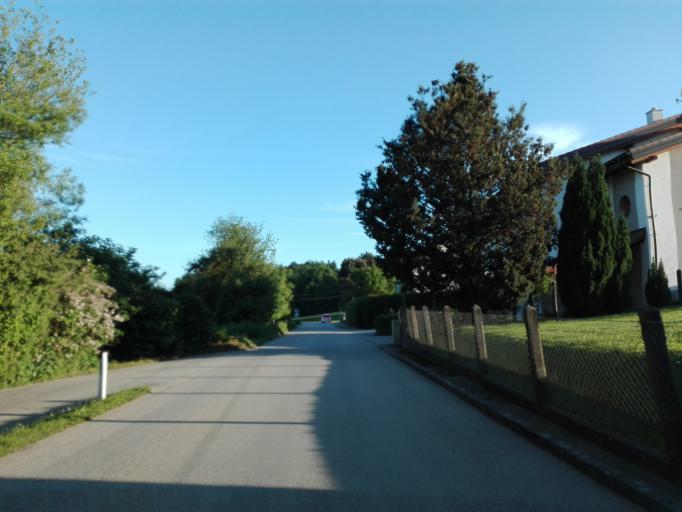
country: AT
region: Upper Austria
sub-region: Politischer Bezirk Urfahr-Umgebung
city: Feldkirchen an der Donau
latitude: 48.3199
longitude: 13.9999
